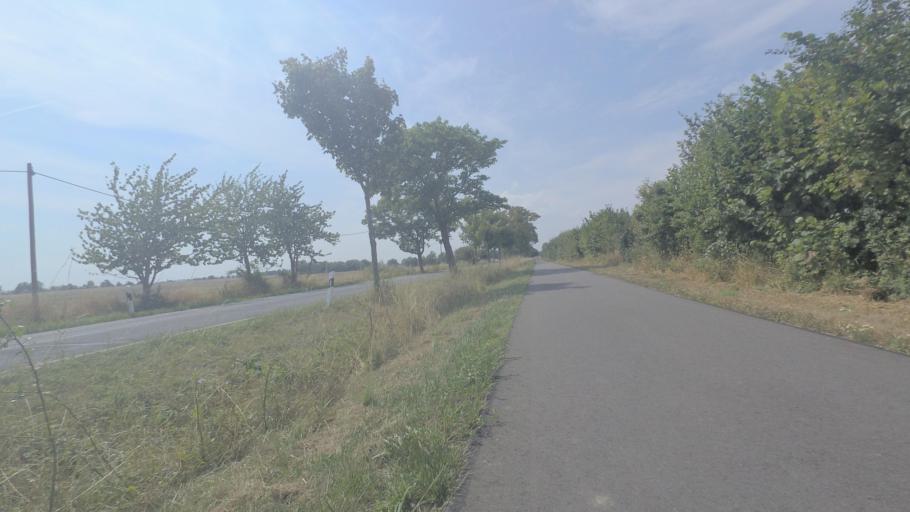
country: DE
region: Mecklenburg-Vorpommern
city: Garz
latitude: 54.2450
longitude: 13.3314
